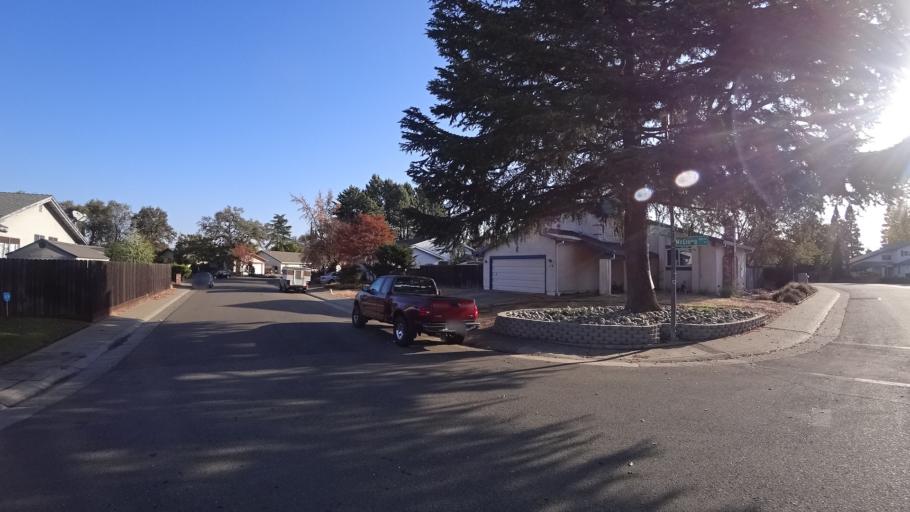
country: US
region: California
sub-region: Sacramento County
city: Citrus Heights
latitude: 38.6960
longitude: -121.2652
